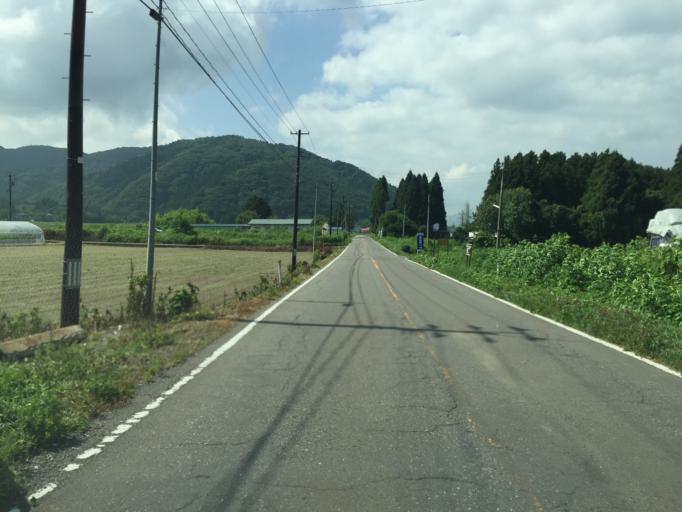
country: JP
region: Fukushima
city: Inawashiro
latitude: 37.4456
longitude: 140.1526
